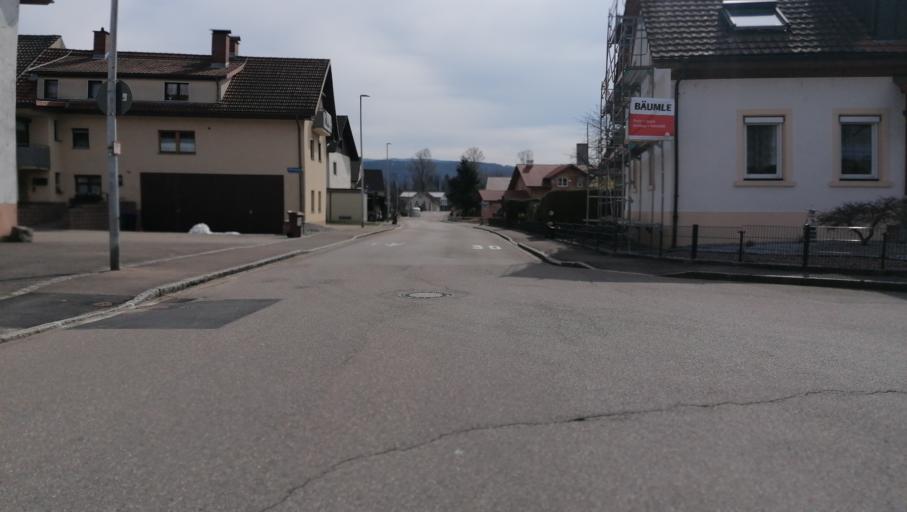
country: CH
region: Aargau
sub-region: Bezirk Rheinfelden
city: Stein
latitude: 47.5601
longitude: 7.9685
